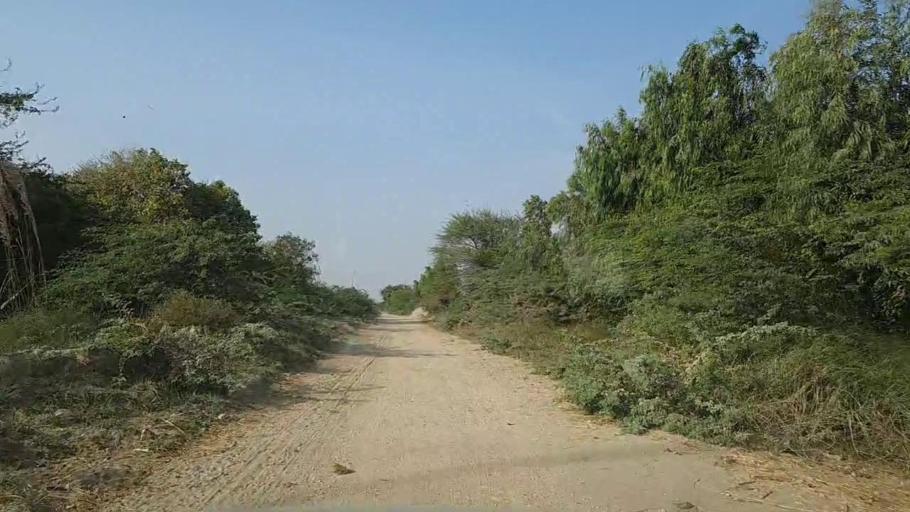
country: PK
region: Sindh
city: Mirpur Sakro
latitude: 24.5903
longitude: 67.6494
